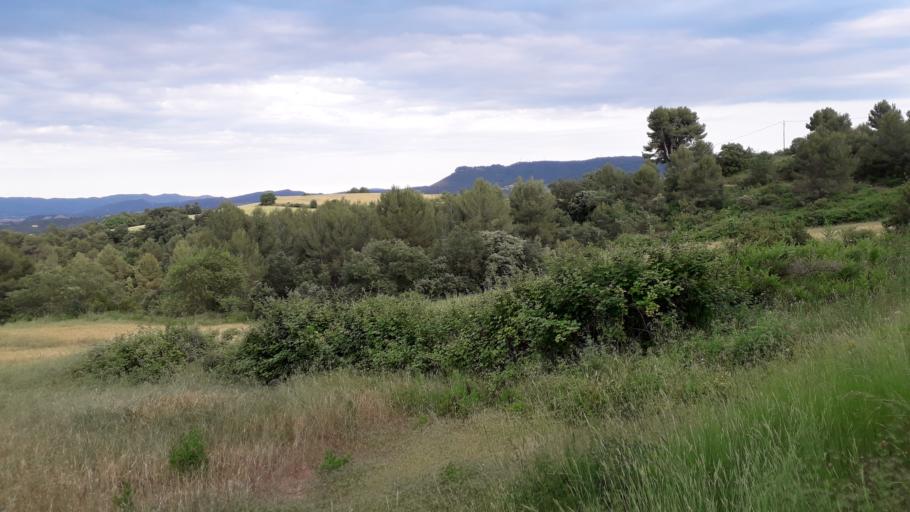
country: ES
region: Catalonia
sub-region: Provincia de Barcelona
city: Jorba
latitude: 41.5879
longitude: 1.5396
